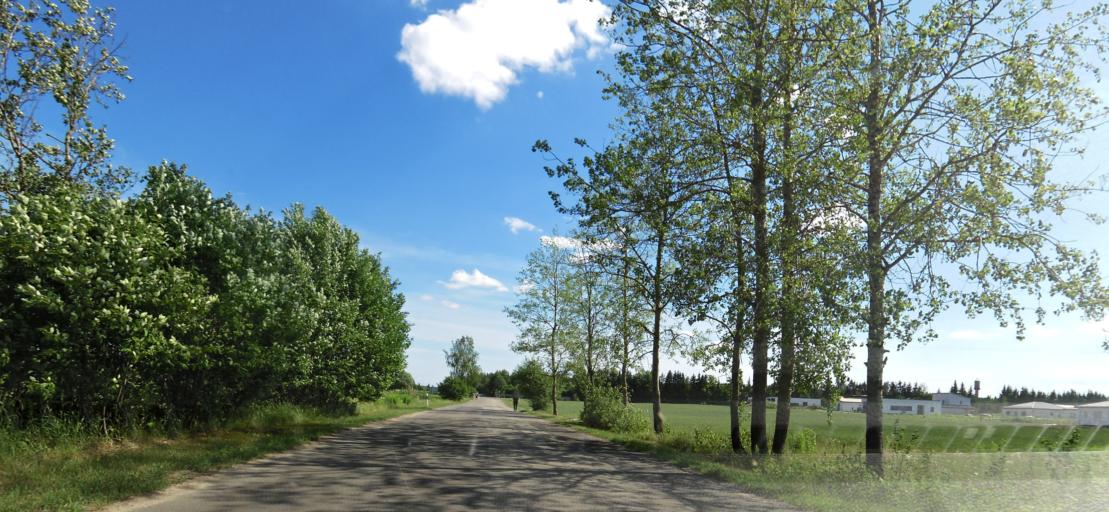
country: LT
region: Vilnius County
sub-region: Vilnius
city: Fabijoniskes
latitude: 54.8085
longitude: 25.3257
